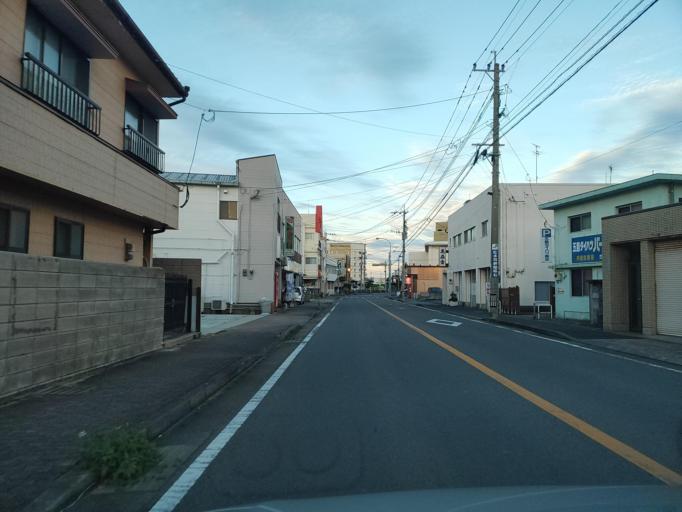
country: JP
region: Nagasaki
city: Fukuecho
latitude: 32.6943
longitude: 128.8449
